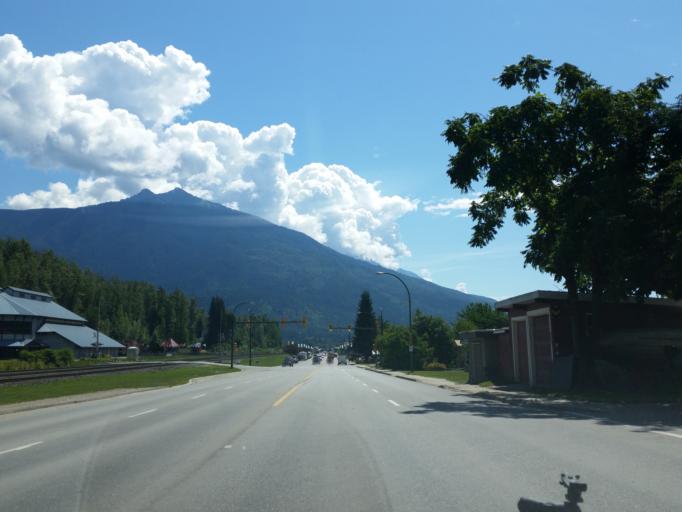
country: CA
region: British Columbia
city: Revelstoke
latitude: 51.0046
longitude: -118.2028
